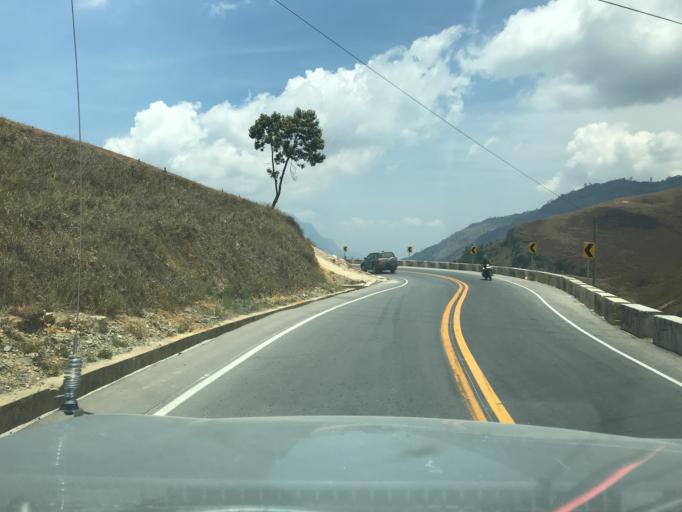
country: TL
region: Manufahi
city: Same
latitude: -8.8803
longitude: 125.6039
